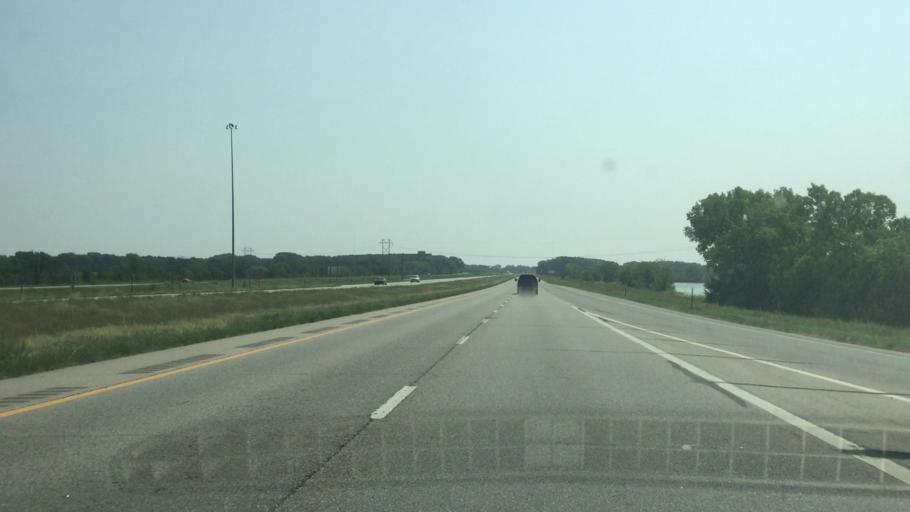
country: US
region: Kansas
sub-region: Lyon County
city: Emporia
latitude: 38.4102
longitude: -96.1350
